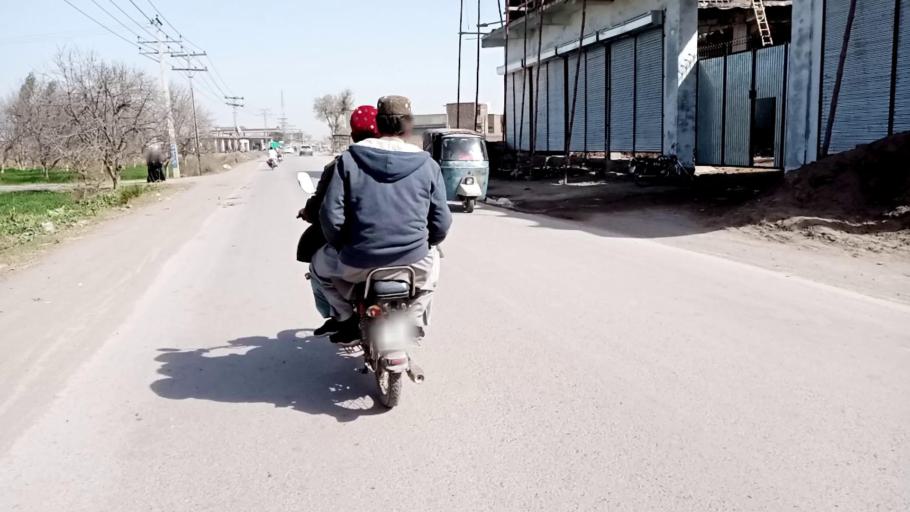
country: PK
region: Khyber Pakhtunkhwa
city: Peshawar
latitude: 34.0002
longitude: 71.6363
